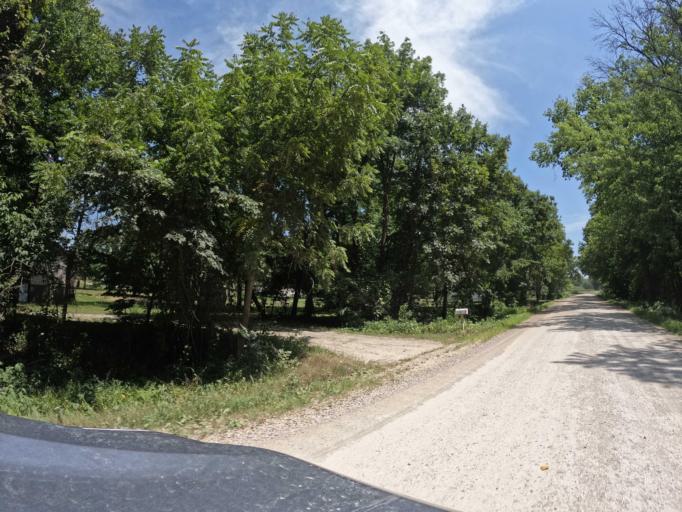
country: US
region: Iowa
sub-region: Henry County
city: Mount Pleasant
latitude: 40.9336
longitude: -91.6092
